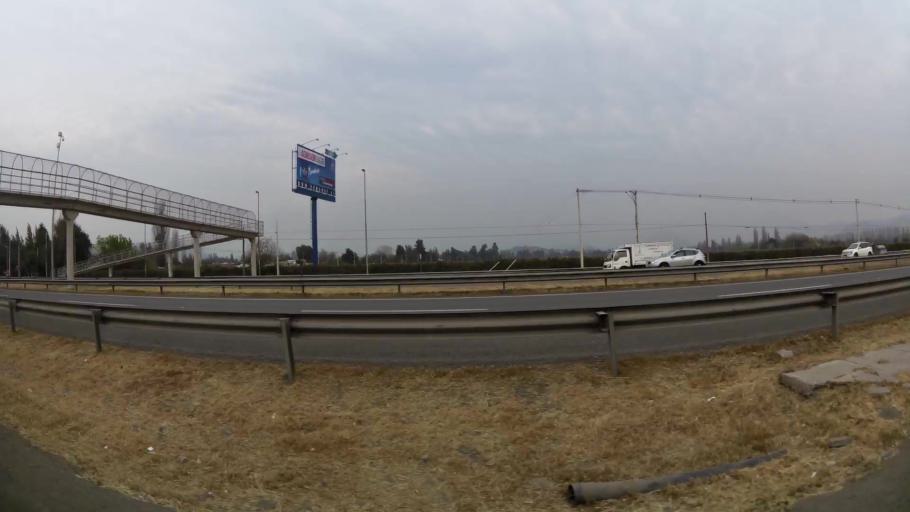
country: CL
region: Santiago Metropolitan
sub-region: Provincia de Chacabuco
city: Chicureo Abajo
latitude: -33.2721
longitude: -70.7011
